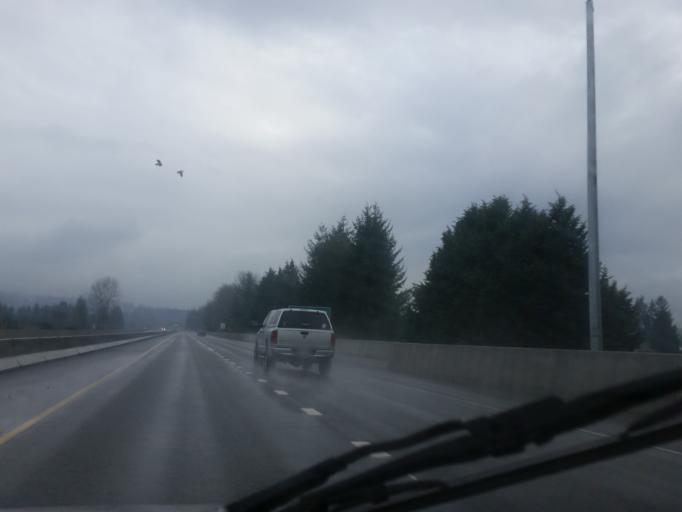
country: US
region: Washington
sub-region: Snohomish County
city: Monroe
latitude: 47.8546
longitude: -121.9954
